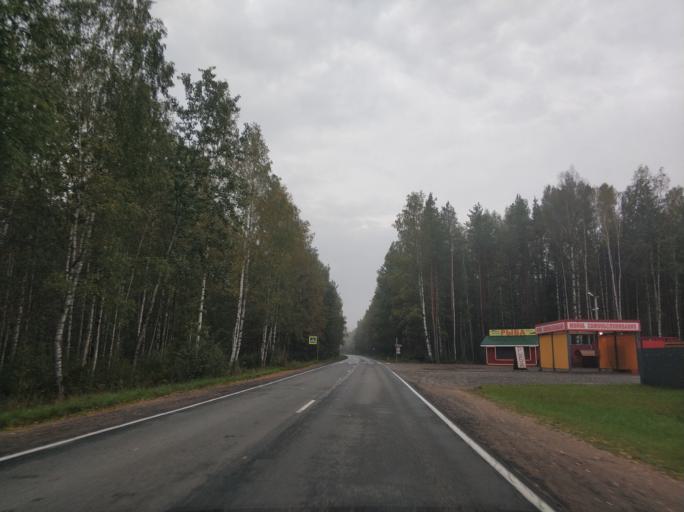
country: RU
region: Leningrad
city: Shcheglovo
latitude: 60.0922
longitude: 30.8548
